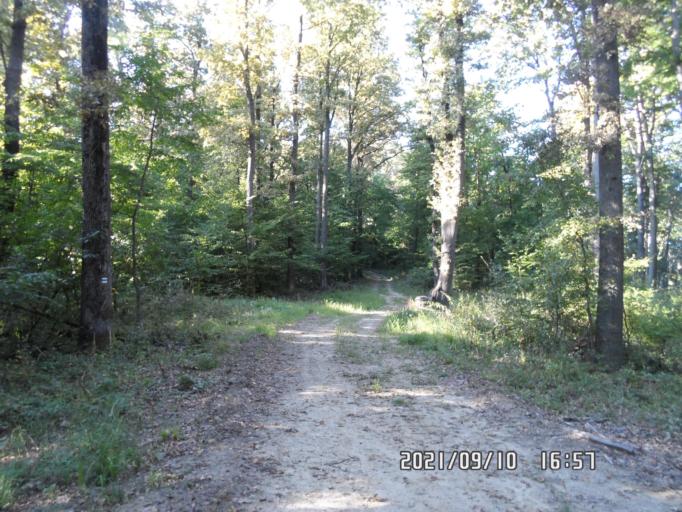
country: HU
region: Zala
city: Nagykanizsa
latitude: 46.5779
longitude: 17.0465
